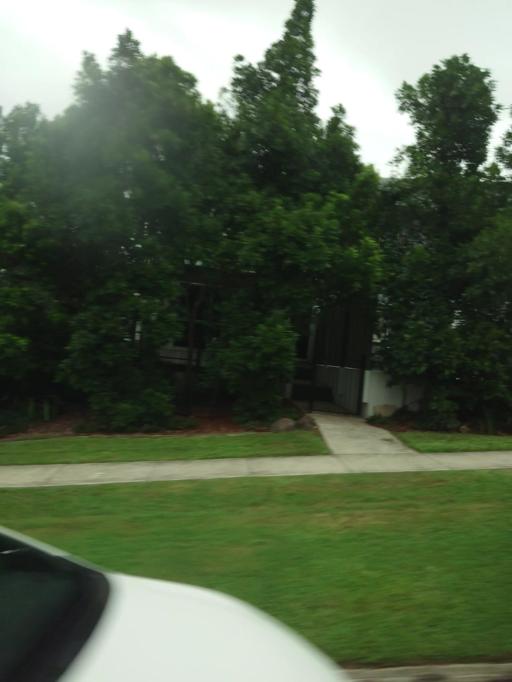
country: AU
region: Queensland
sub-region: Brisbane
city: Morningside
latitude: -27.4718
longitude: 153.0727
